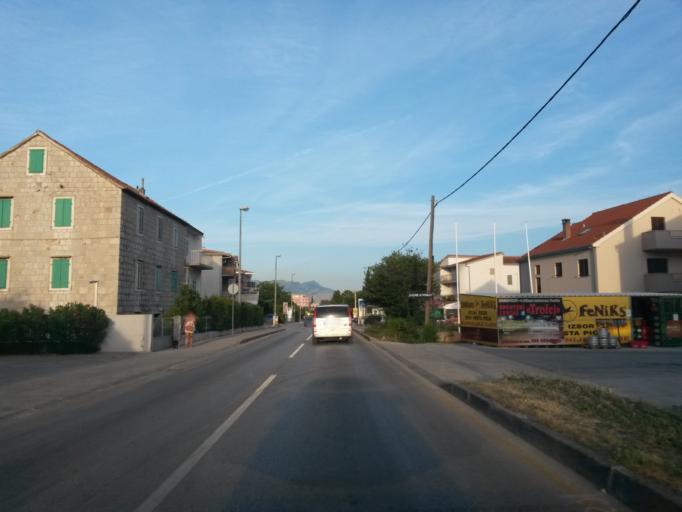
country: HR
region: Splitsko-Dalmatinska
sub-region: Grad Split
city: Split
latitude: 43.5512
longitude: 16.3794
